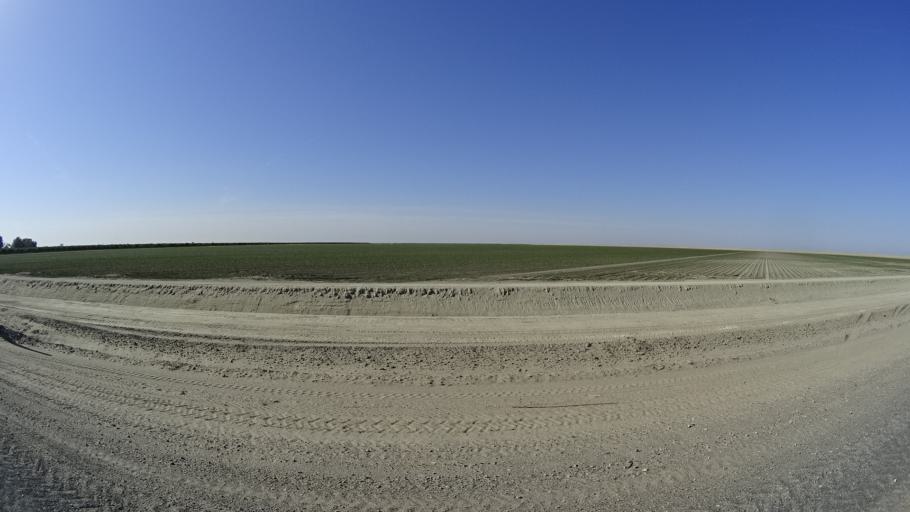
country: US
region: California
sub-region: Kings County
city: Corcoran
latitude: 36.0980
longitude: -119.6017
